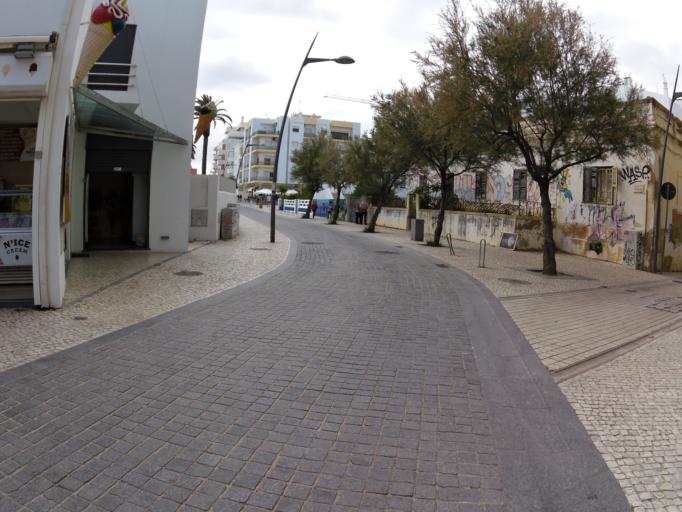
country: PT
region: Faro
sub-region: Silves
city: Armacao de Pera
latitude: 37.1012
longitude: -8.3603
